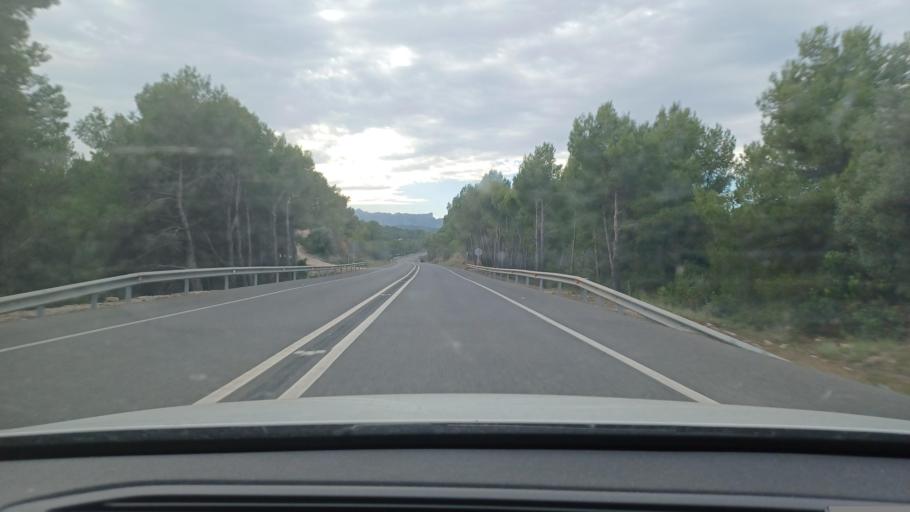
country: ES
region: Catalonia
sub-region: Provincia de Tarragona
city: l'Ametlla de Mar
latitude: 40.8948
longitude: 0.7684
